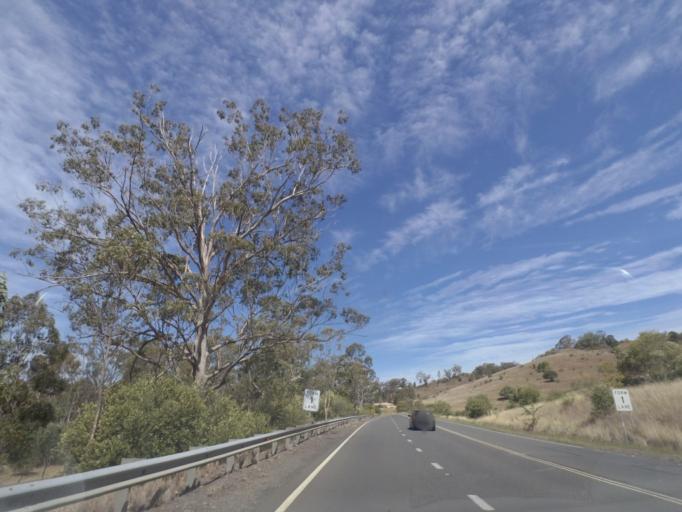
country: AU
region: New South Wales
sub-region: Wollondilly
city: Picton
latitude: -34.1646
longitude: 150.6218
